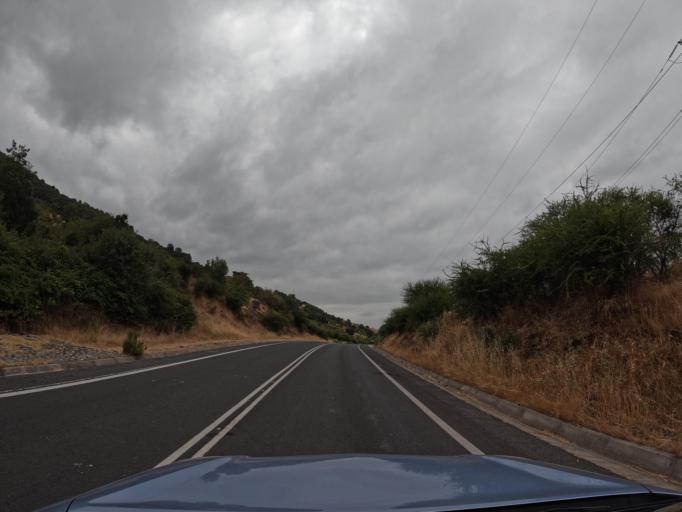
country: CL
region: O'Higgins
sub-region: Provincia de Colchagua
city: Chimbarongo
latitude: -34.7368
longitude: -71.1152
